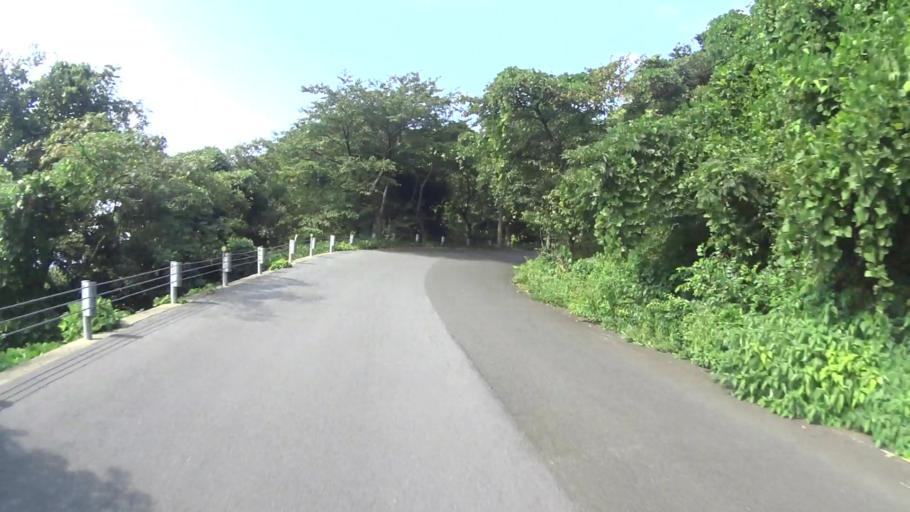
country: JP
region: Kyoto
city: Miyazu
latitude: 35.7701
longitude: 135.2262
